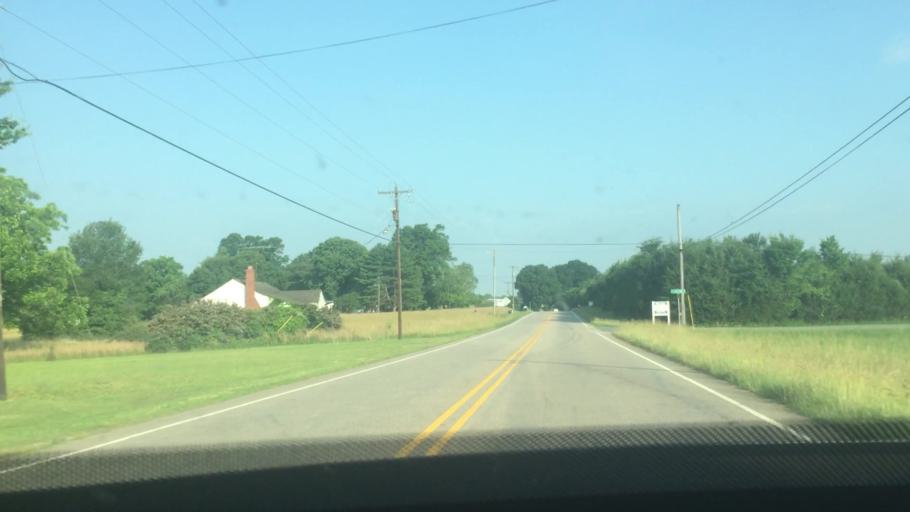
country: US
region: North Carolina
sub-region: Rowan County
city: Enochville
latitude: 35.5808
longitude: -80.7188
